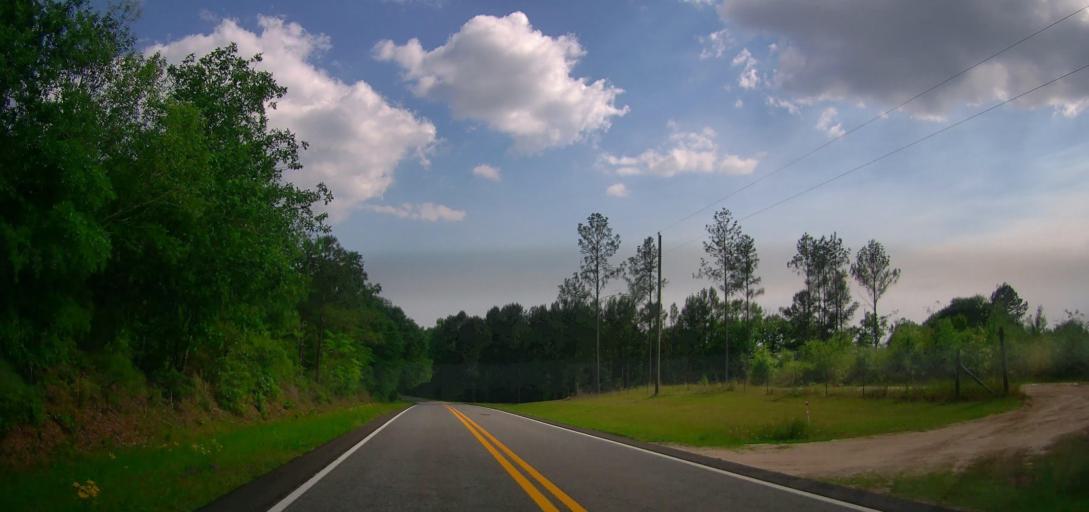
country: US
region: Georgia
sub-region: Laurens County
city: East Dublin
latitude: 32.6351
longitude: -82.8942
